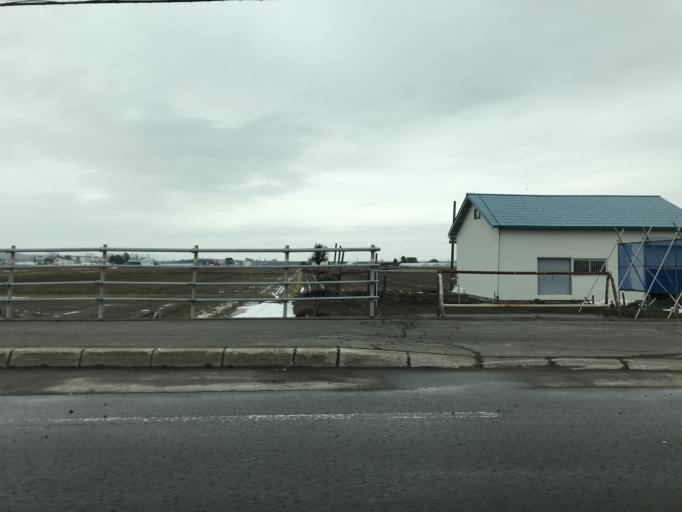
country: JP
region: Hokkaido
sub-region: Asahikawa-shi
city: Asahikawa
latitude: 43.8297
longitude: 142.4228
